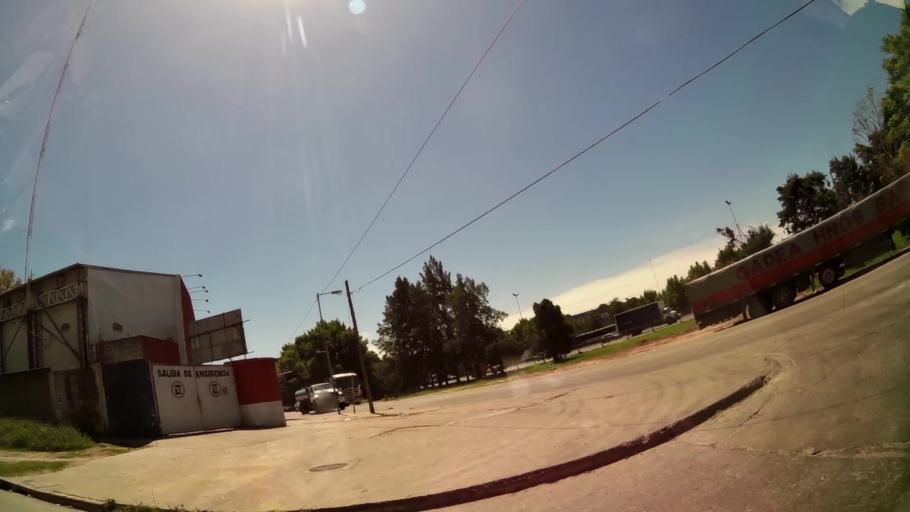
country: AR
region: Buenos Aires
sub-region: Partido de Tigre
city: Tigre
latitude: -34.4806
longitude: -58.6459
